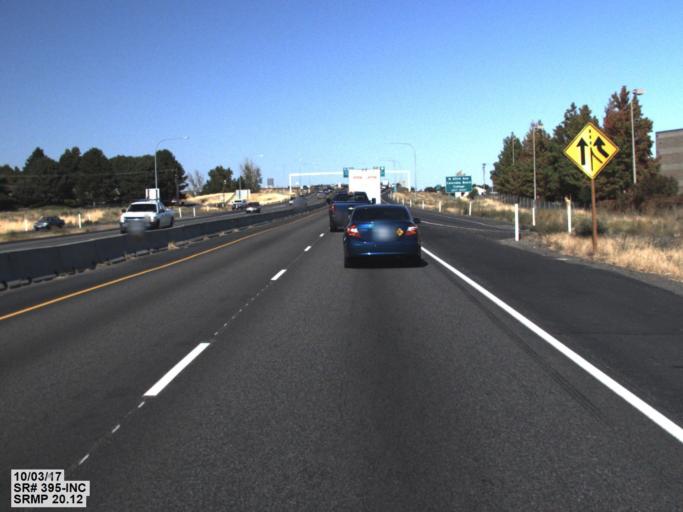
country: US
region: Washington
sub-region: Franklin County
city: Pasco
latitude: 46.2426
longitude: -119.1282
